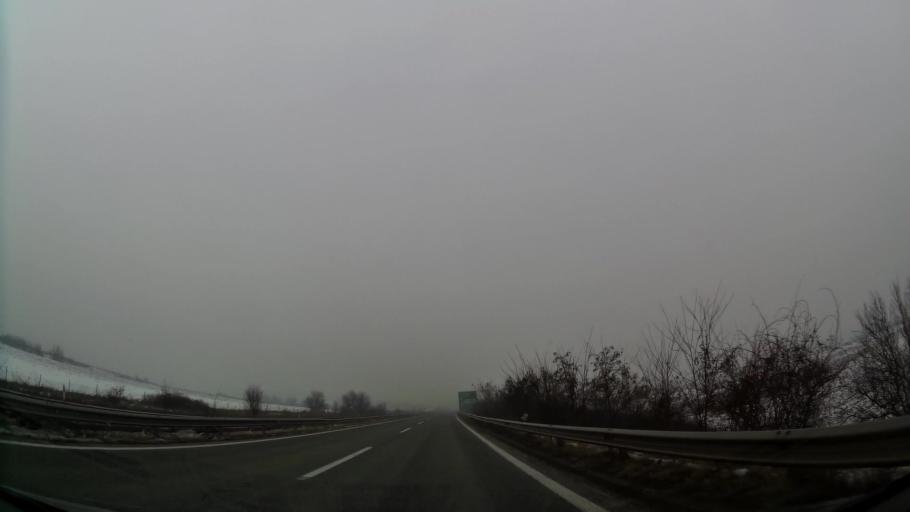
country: MK
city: Miladinovci
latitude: 41.9692
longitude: 21.6444
